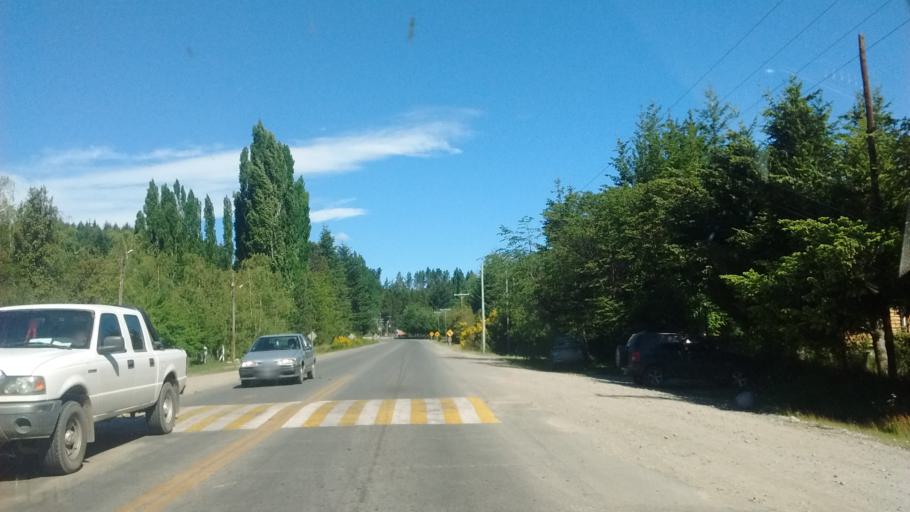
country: AR
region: Chubut
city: Lago Puelo
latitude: -42.0332
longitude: -71.5658
